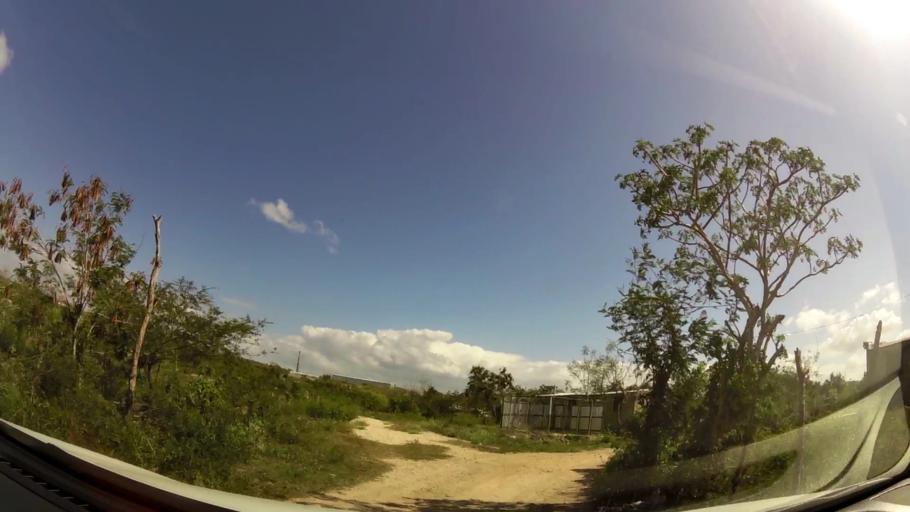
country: DO
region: Santo Domingo
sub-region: Santo Domingo
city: Boca Chica
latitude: 18.4624
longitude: -69.6276
